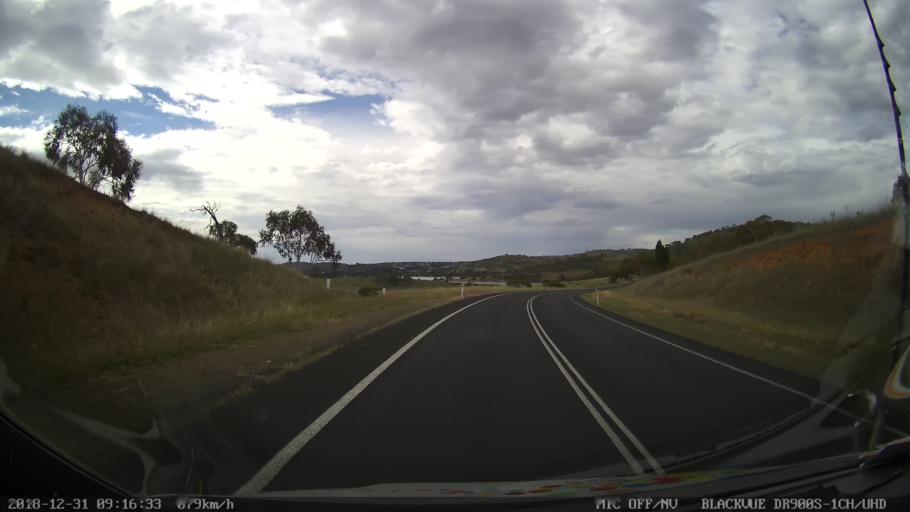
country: AU
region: New South Wales
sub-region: Snowy River
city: Jindabyne
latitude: -36.3970
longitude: 148.5969
